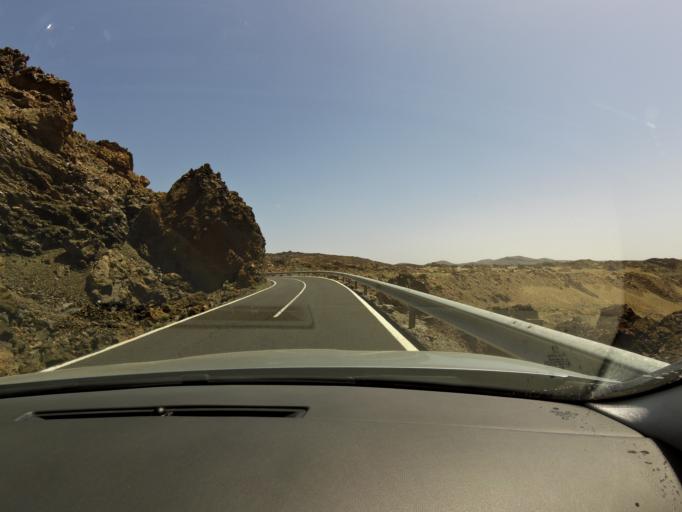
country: ES
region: Canary Islands
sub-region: Provincia de Santa Cruz de Tenerife
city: Los Realejos
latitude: 28.2613
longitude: -16.5925
